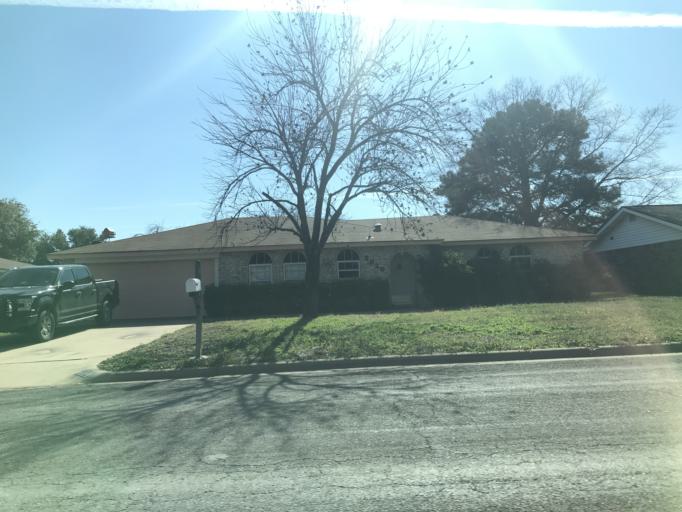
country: US
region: Texas
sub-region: Tom Green County
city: San Angelo
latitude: 31.4311
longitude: -100.4903
